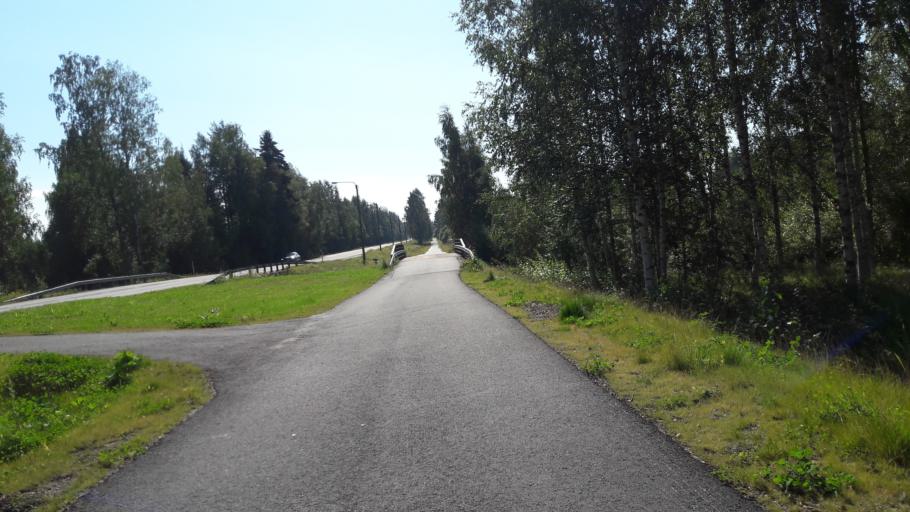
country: FI
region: North Karelia
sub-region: Joensuu
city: Joensuu
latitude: 62.5554
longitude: 29.8215
